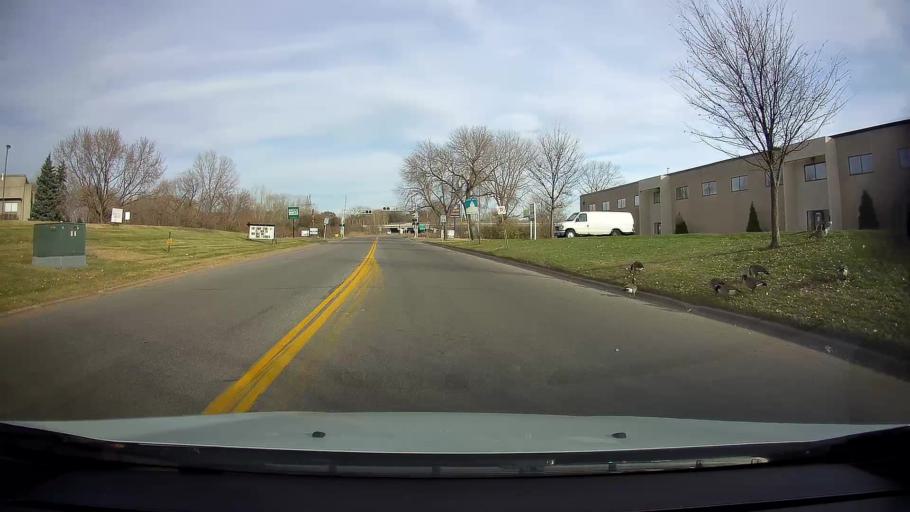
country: US
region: Minnesota
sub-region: Ramsey County
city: Lauderdale
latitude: 44.9772
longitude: -93.2069
